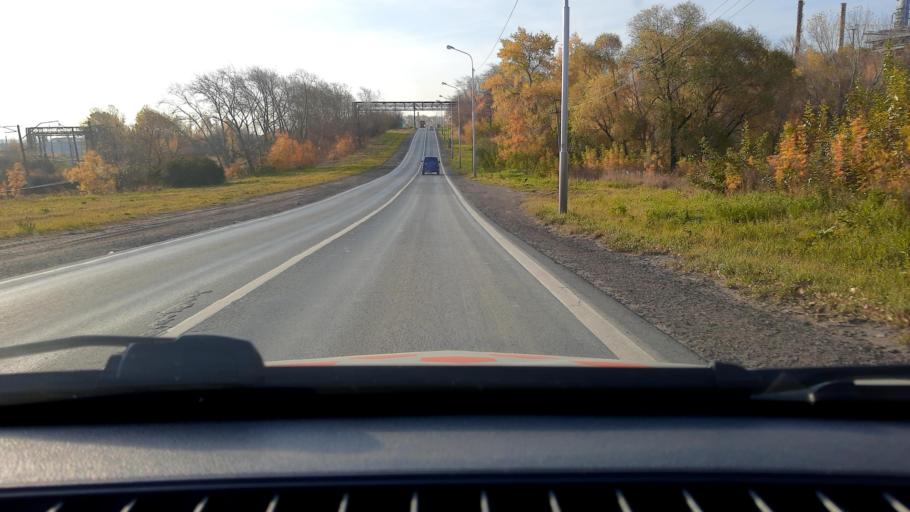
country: RU
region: Bashkortostan
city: Ufa
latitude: 54.8847
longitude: 56.0941
